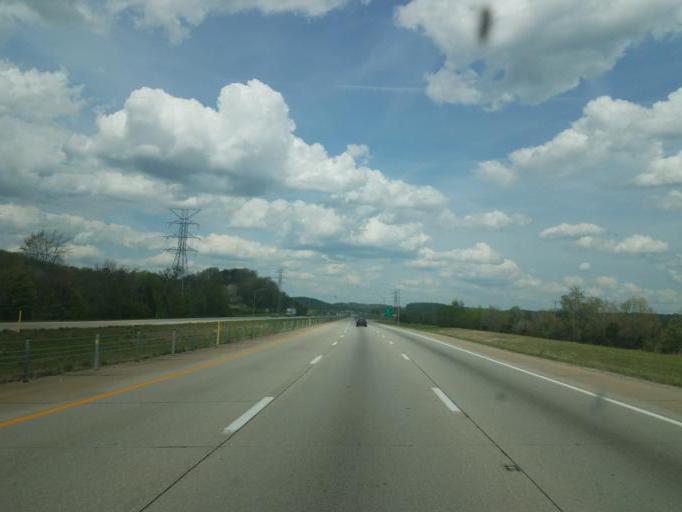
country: US
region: Kentucky
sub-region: Bullitt County
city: Shepherdsville
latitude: 37.9170
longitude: -85.6870
